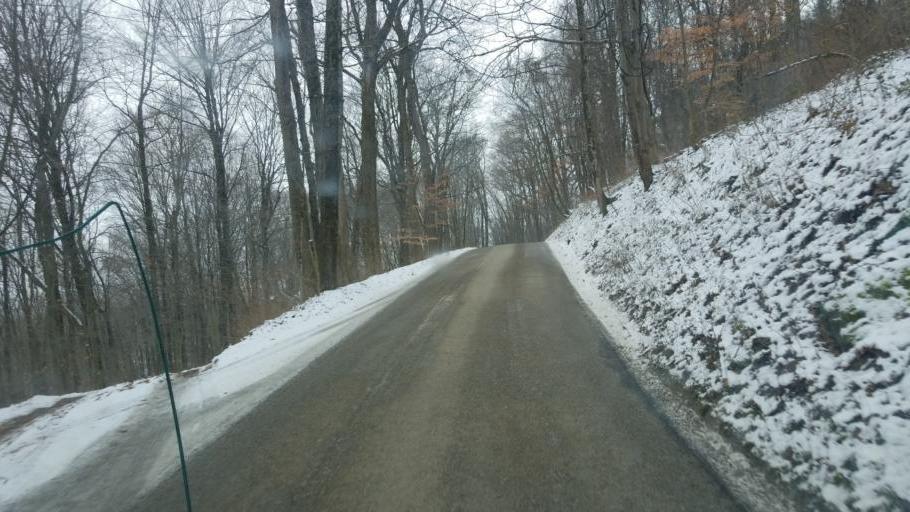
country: US
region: Ohio
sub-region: Sandusky County
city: Bellville
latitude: 40.6106
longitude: -82.4967
